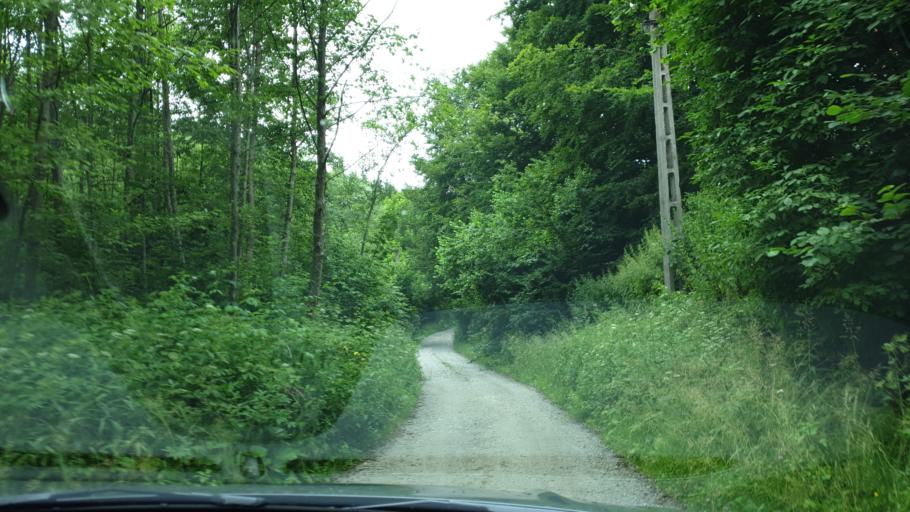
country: RO
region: Hunedoara
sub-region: Comuna Uricani
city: Uricani
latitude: 45.3020
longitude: 22.9898
